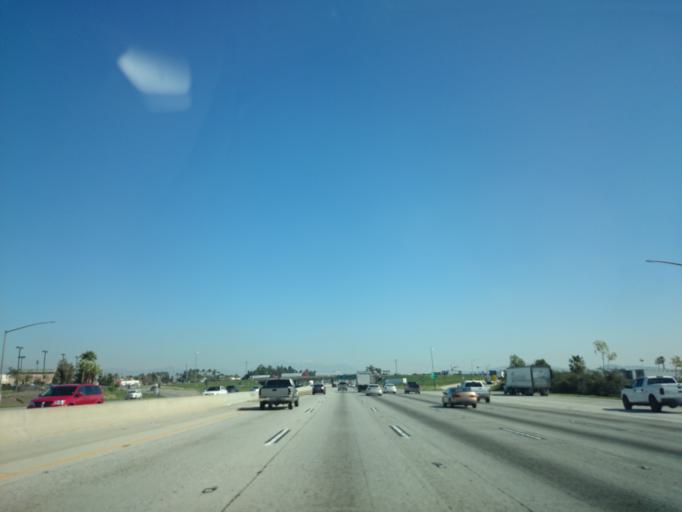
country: US
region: California
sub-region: San Bernardino County
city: Rancho Cucamonga
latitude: 34.0674
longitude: -117.5630
